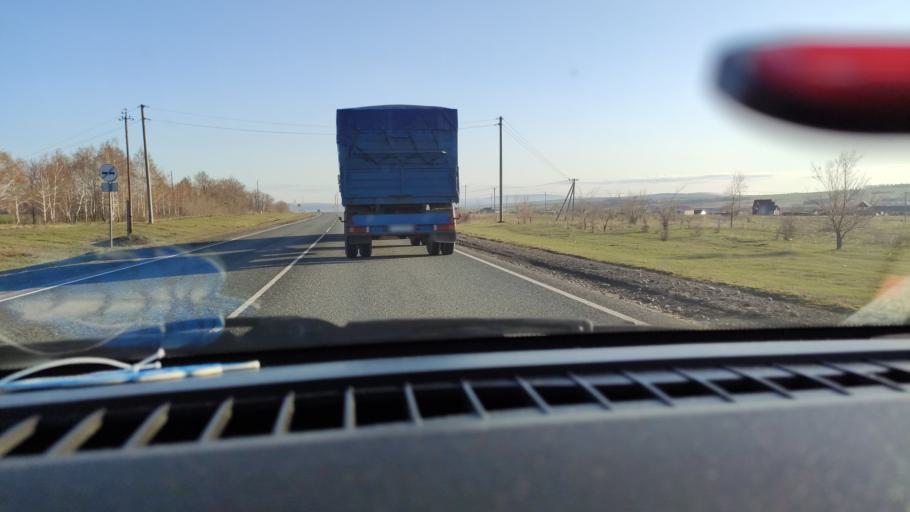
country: RU
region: Saratov
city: Balakovo
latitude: 52.1127
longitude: 47.7498
